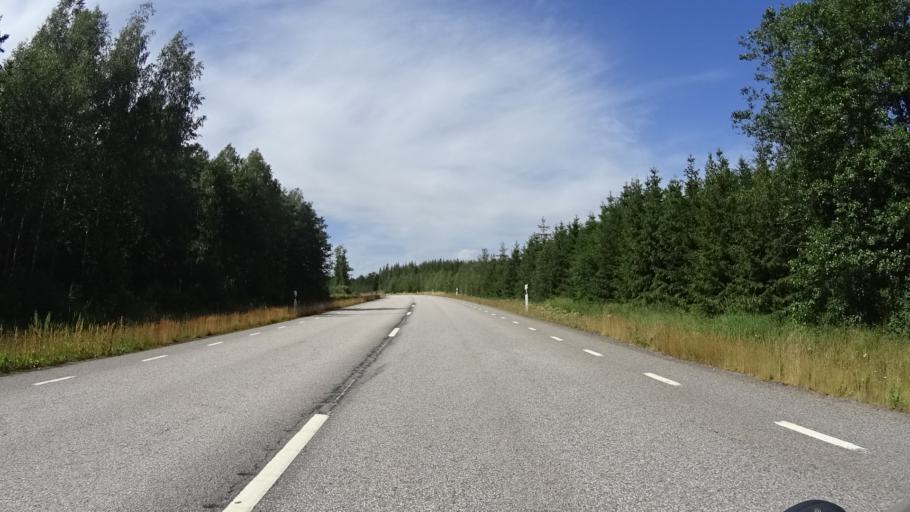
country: SE
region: Kalmar
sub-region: Vasterviks Kommun
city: Gamleby
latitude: 57.9527
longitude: 16.3778
